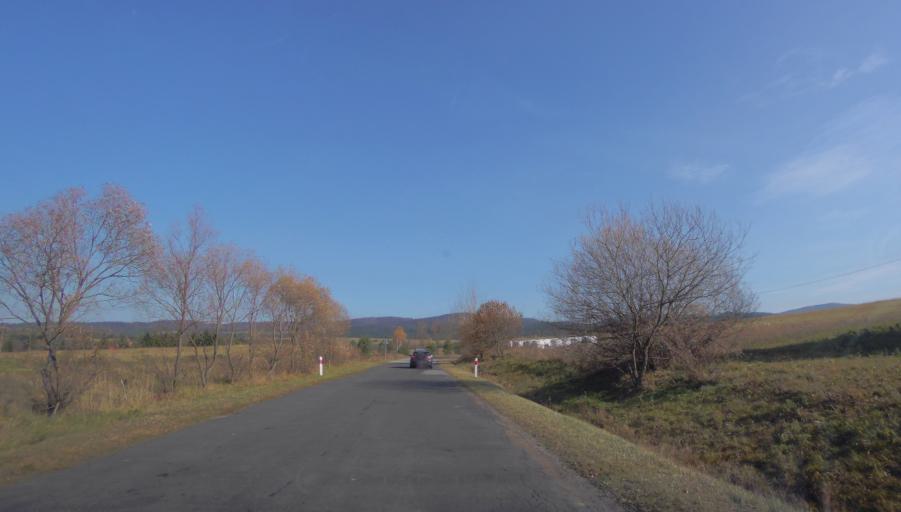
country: PL
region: Subcarpathian Voivodeship
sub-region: Powiat sanocki
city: Komancza
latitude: 49.2476
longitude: 22.1184
